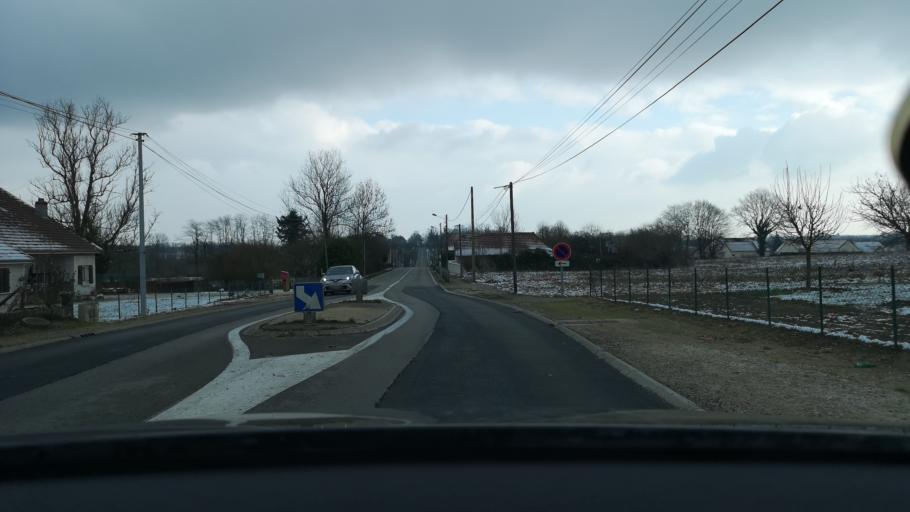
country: FR
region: Bourgogne
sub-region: Departement de Saone-et-Loire
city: Saint-Martin-en-Bresse
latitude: 46.7415
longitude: 5.0980
